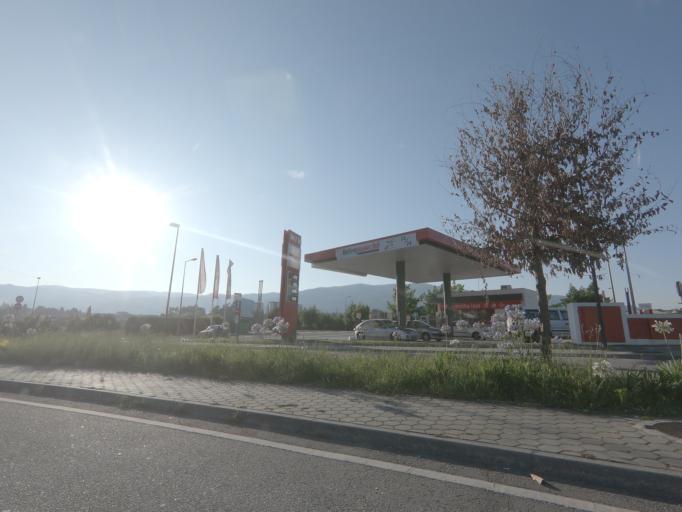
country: PT
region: Vila Real
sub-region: Vila Real
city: Vila Real
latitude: 41.3100
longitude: -7.7243
